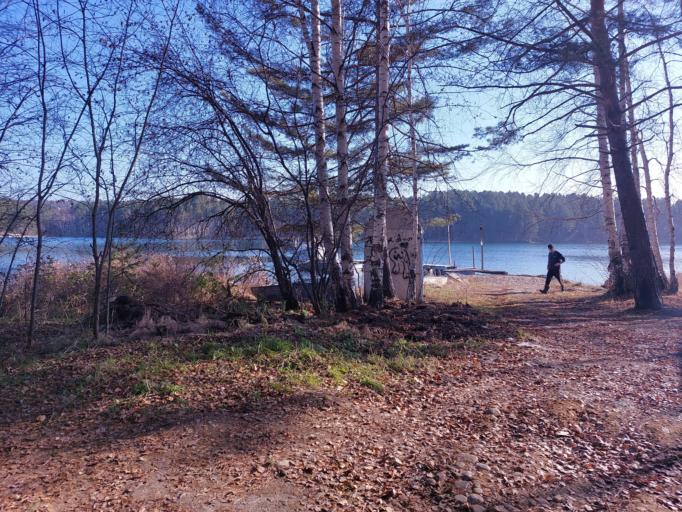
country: RU
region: Irkutsk
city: Pivovarikha
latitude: 52.1867
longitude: 104.4645
